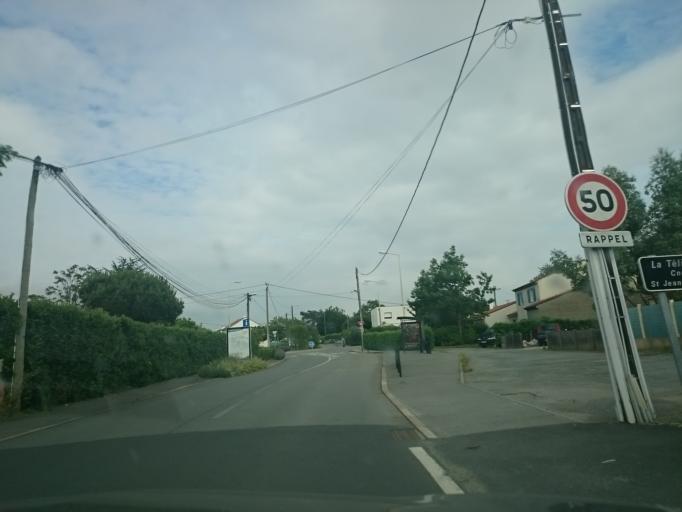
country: FR
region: Pays de la Loire
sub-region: Departement de la Loire-Atlantique
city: Le Pellerin
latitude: 47.1960
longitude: -1.7416
